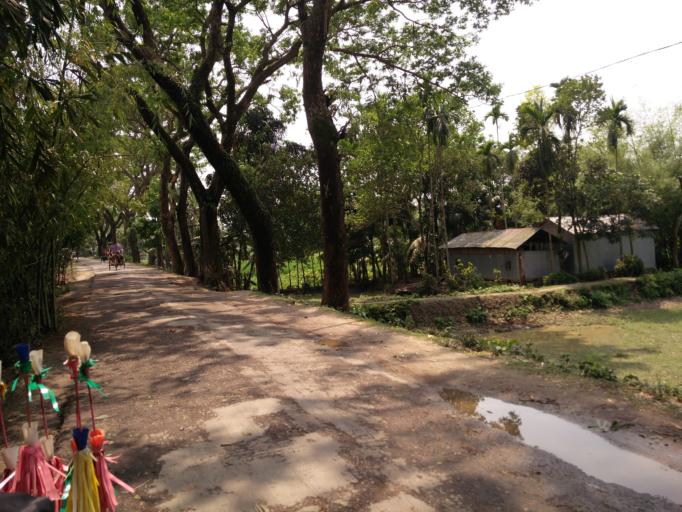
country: BD
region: Dhaka
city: Sherpur
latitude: 24.9416
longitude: 90.1600
